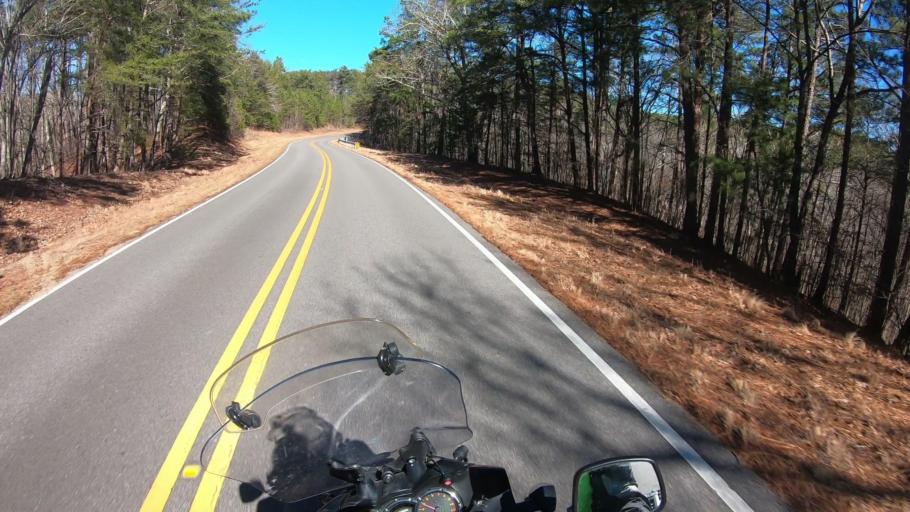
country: US
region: Alabama
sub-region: Calhoun County
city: Oxford
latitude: 33.4946
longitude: -85.7753
